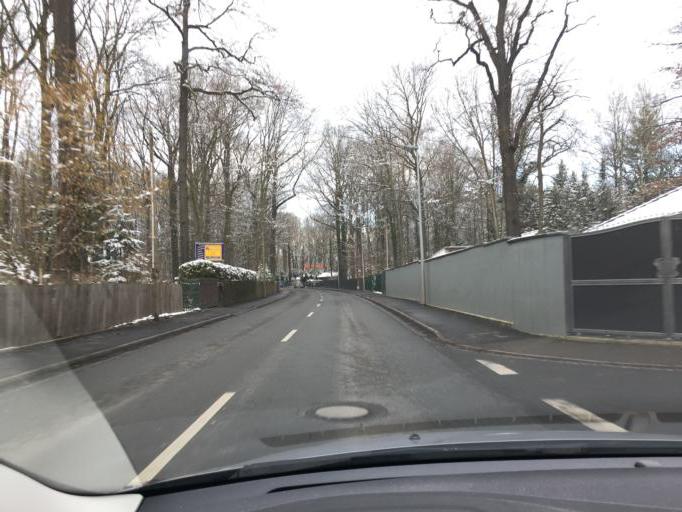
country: DE
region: Saxony
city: Brandis
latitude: 51.3134
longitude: 12.5976
